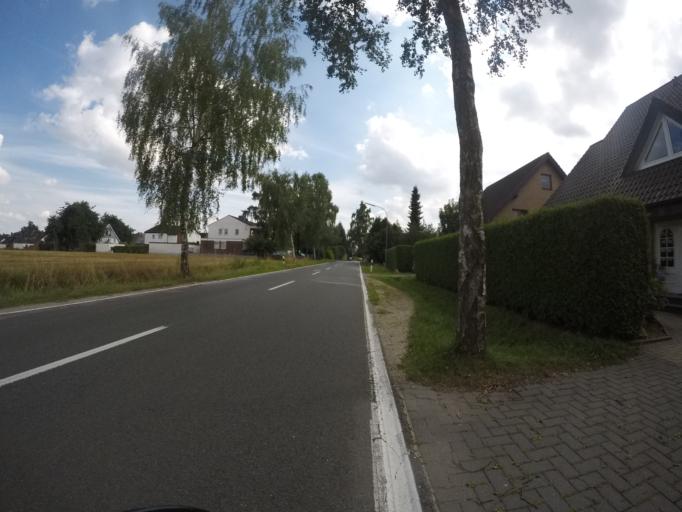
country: DE
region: North Rhine-Westphalia
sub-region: Regierungsbezirk Detmold
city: Herford
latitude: 52.0842
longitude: 8.6076
